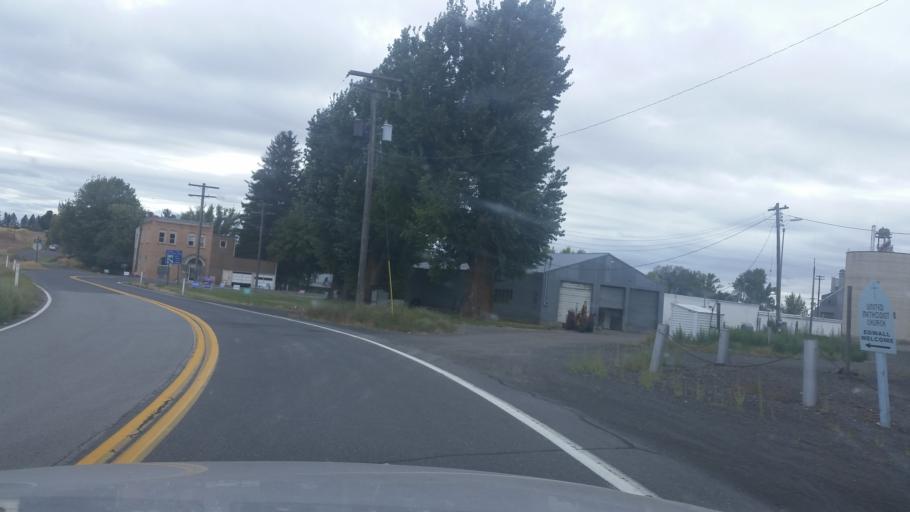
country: US
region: Washington
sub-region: Lincoln County
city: Davenport
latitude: 47.5066
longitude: -117.9495
